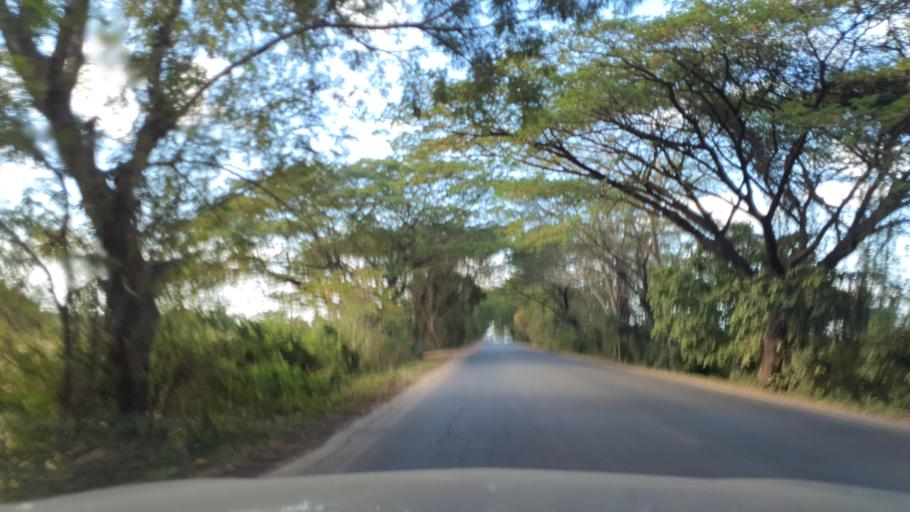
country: TH
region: Nakhon Phanom
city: Ban Phaeng
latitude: 18.0229
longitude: 104.1482
